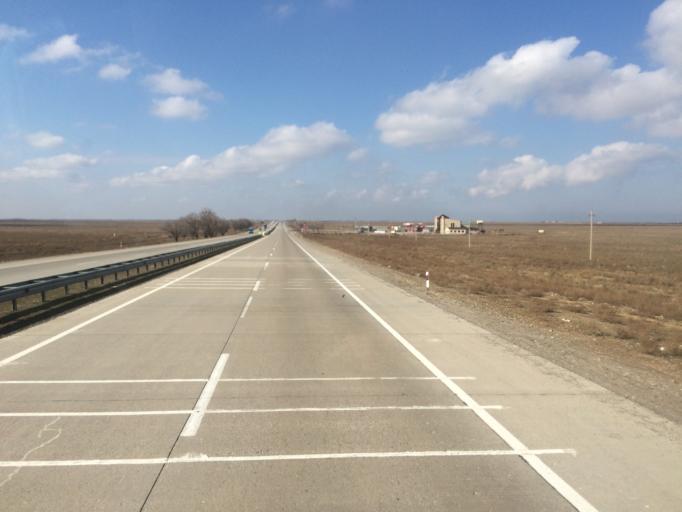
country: KZ
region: Ongtustik Qazaqstan
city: Temirlanovka
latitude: 42.8383
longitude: 69.1110
